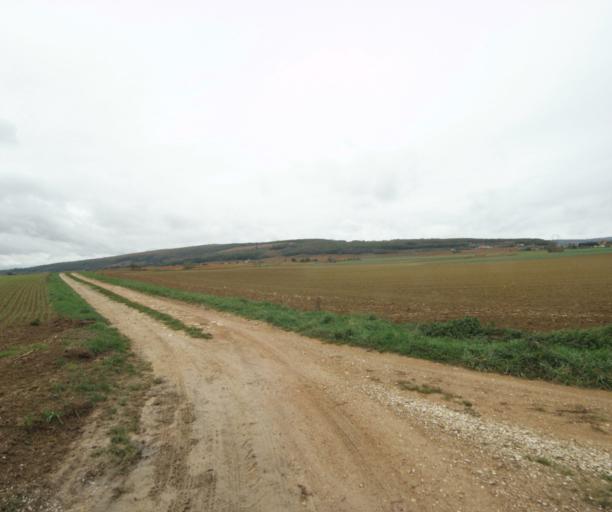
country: FR
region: Rhone-Alpes
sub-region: Departement de l'Ain
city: Pont-de-Vaux
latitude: 46.4627
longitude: 4.8666
